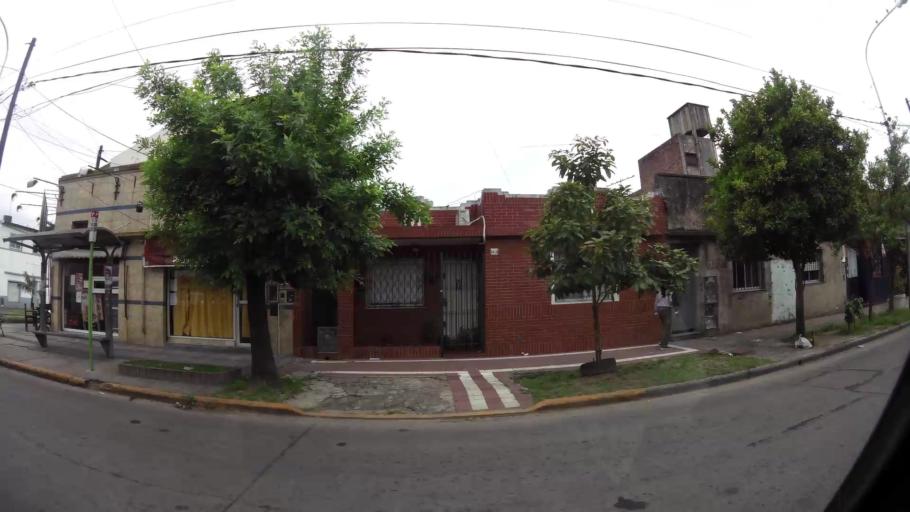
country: AR
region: Buenos Aires
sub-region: Partido de Avellaneda
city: Avellaneda
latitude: -34.6882
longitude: -58.3689
